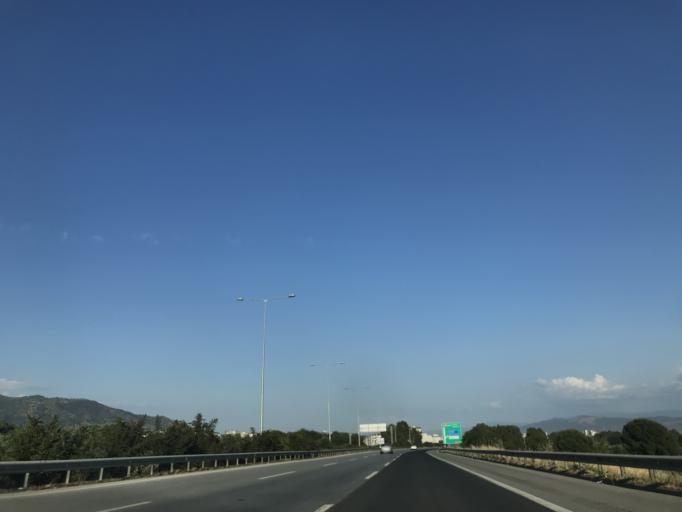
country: TR
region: Aydin
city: Aydin
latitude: 37.8593
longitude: 27.7935
